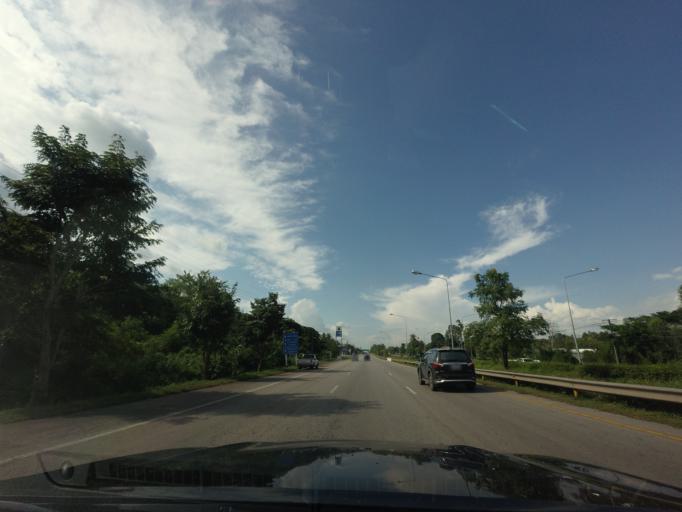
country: TH
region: Nong Khai
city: Sa Khrai
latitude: 17.7662
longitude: 102.7687
